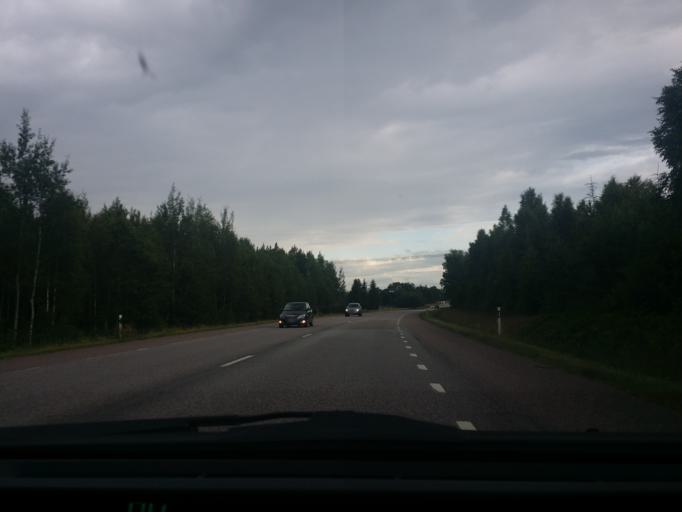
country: SE
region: OErebro
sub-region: Orebro Kommun
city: Hovsta
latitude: 59.4336
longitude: 15.1641
